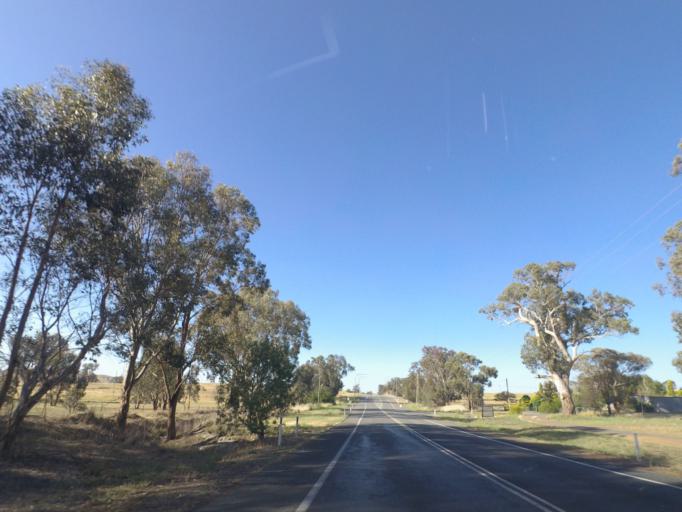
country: AU
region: New South Wales
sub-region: Wagga Wagga
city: Forest Hill
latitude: -35.2696
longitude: 147.7450
